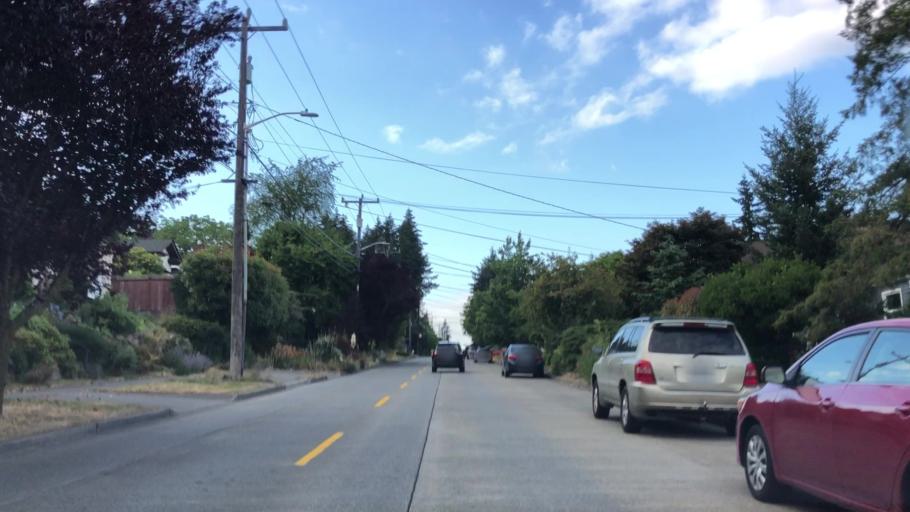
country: US
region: Washington
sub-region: King County
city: Shoreline
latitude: 47.6888
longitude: -122.3122
